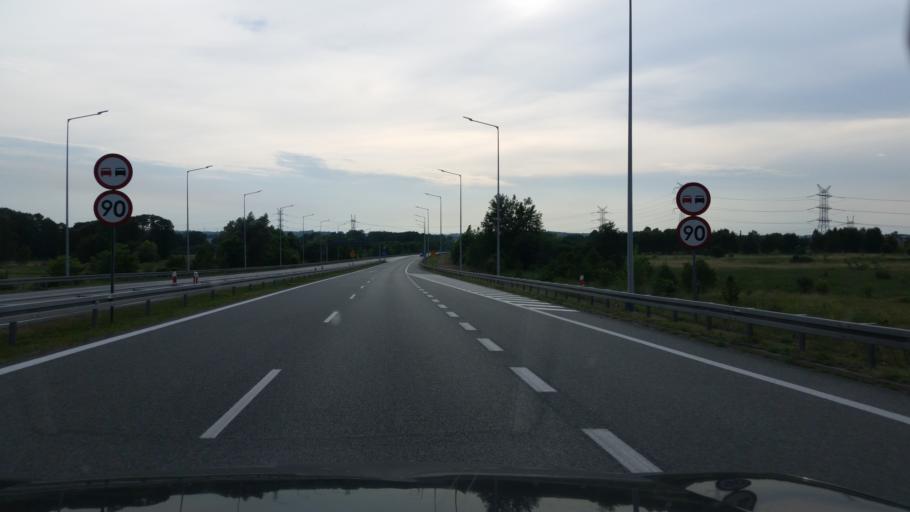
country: PL
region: Silesian Voivodeship
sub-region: Powiat bedzinski
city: Siewierz
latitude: 50.4203
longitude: 19.2011
